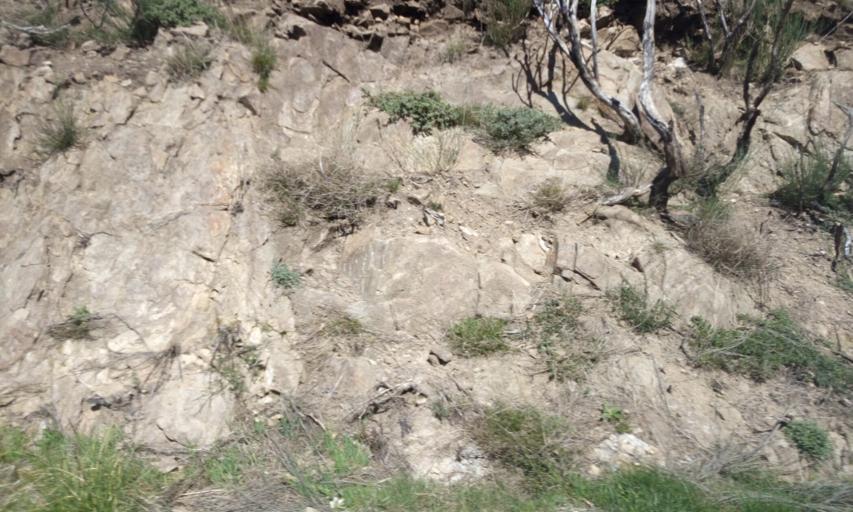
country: PT
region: Guarda
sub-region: Manteigas
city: Manteigas
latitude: 40.4869
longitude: -7.5501
